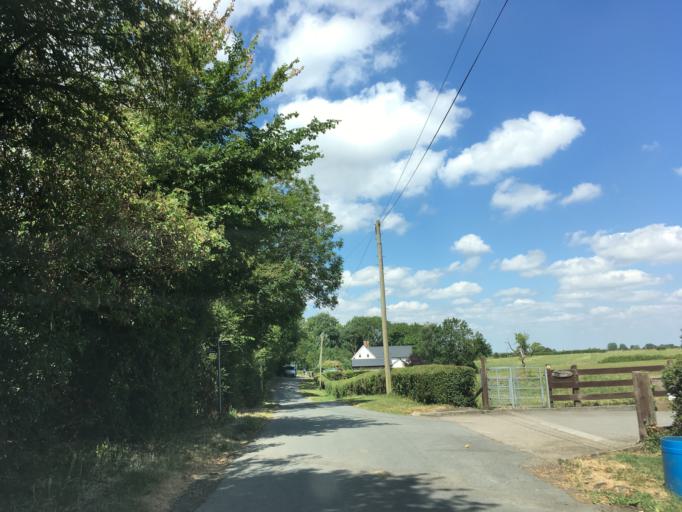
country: GB
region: England
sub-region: Gloucestershire
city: Shurdington
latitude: 51.8479
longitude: -2.1203
